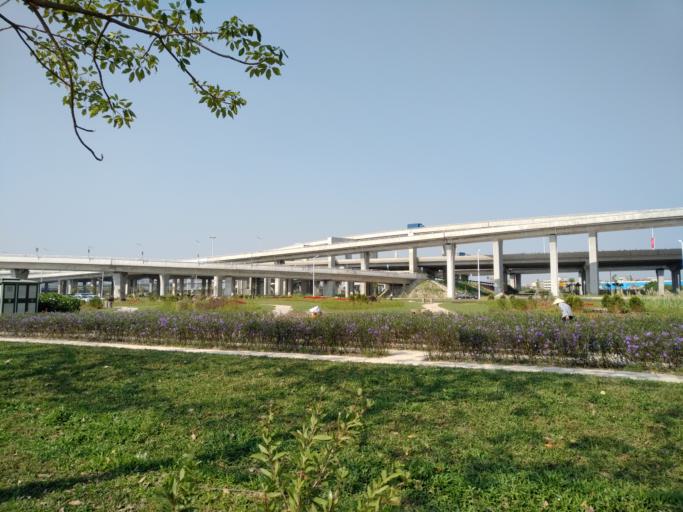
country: CN
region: Guangdong
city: Lile
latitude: 22.5198
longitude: 113.0639
